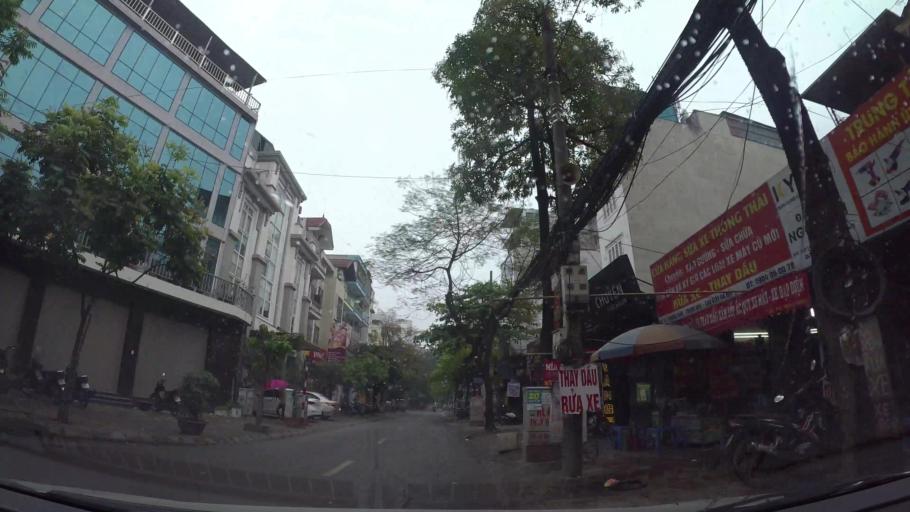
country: VN
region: Ha Noi
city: Cau Giay
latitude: 21.0140
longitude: 105.7970
